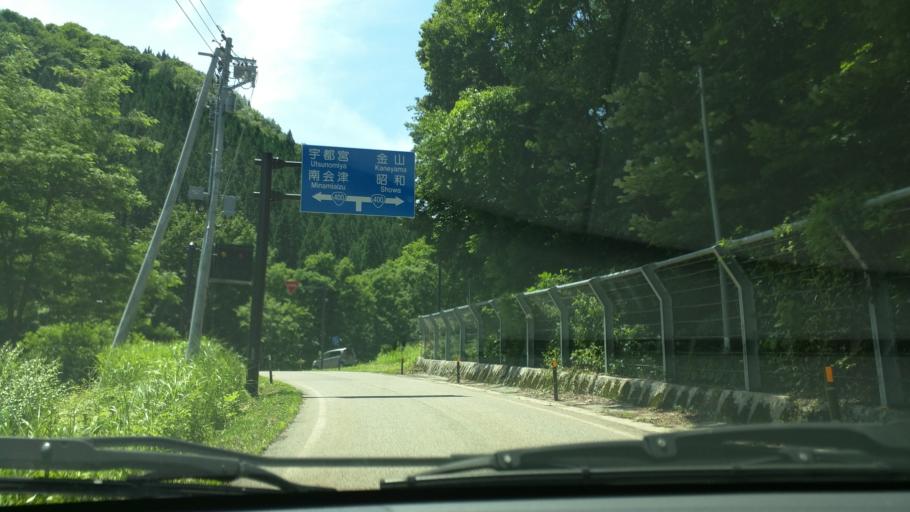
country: JP
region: Fukushima
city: Kitakata
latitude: 37.2553
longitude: 139.7429
